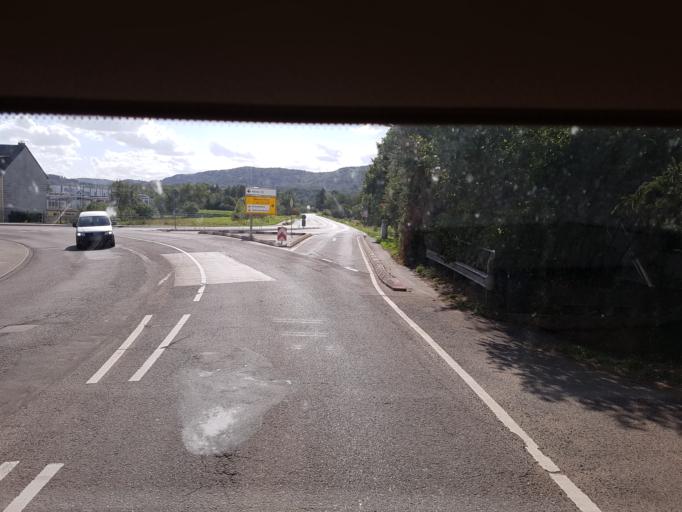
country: DE
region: Rheinland-Pfalz
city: Konz
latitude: 49.6980
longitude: 6.5672
